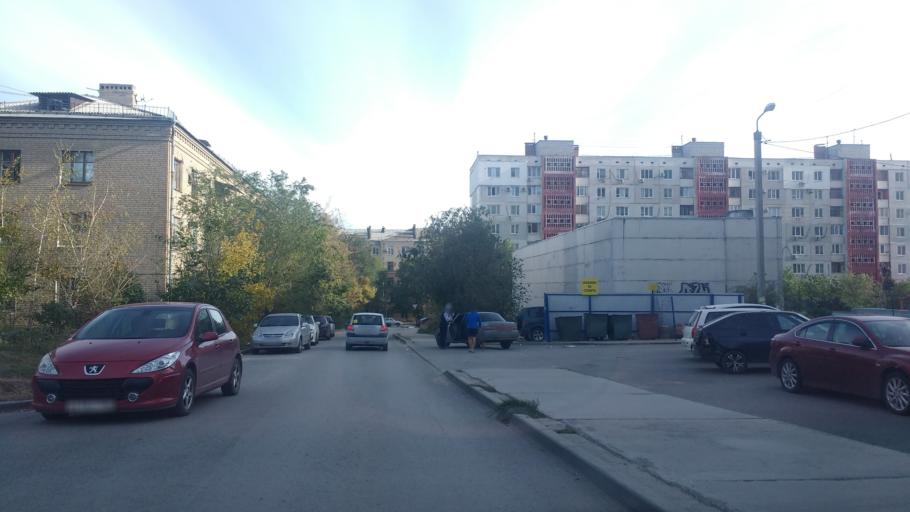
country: RU
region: Volgograd
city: Krasnoslobodsk
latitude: 48.7631
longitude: 44.5536
